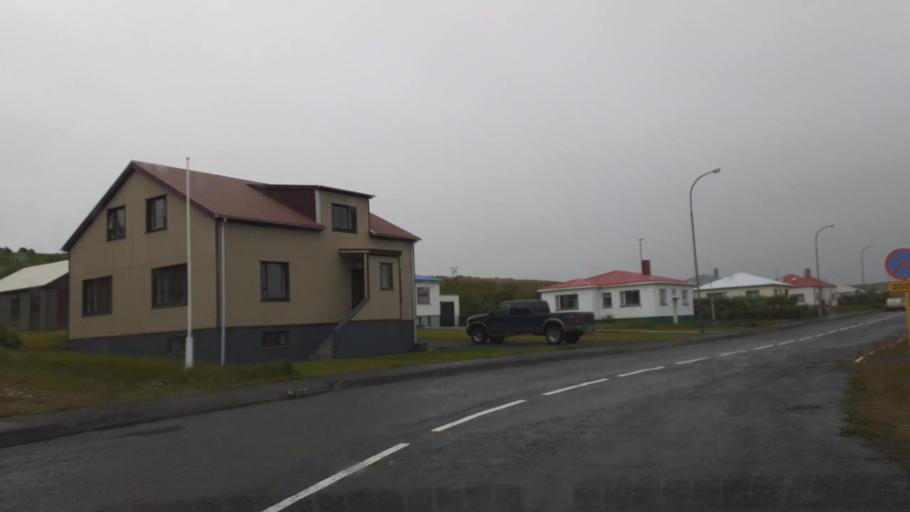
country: IS
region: Northeast
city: Husavik
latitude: 66.4543
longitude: -15.9519
